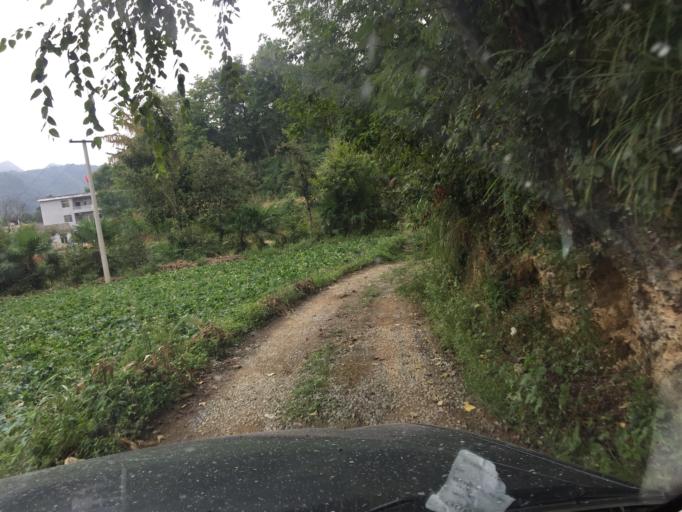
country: CN
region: Guizhou Sheng
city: Nangan
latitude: 28.2470
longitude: 107.9460
